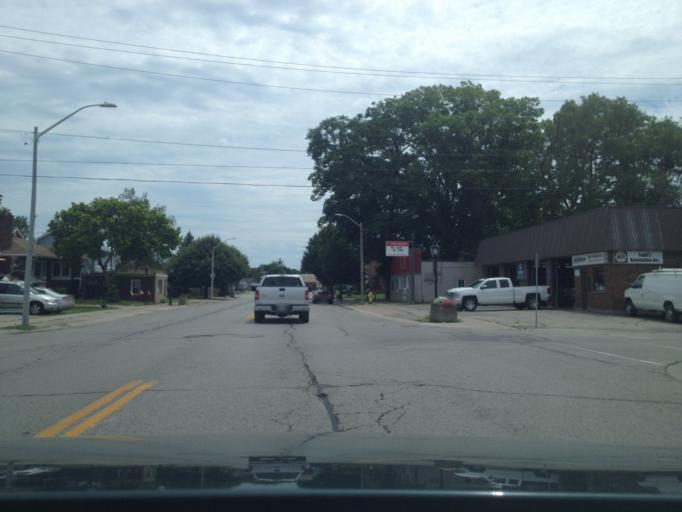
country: CA
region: Ontario
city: Norfolk County
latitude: 42.8551
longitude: -80.4962
